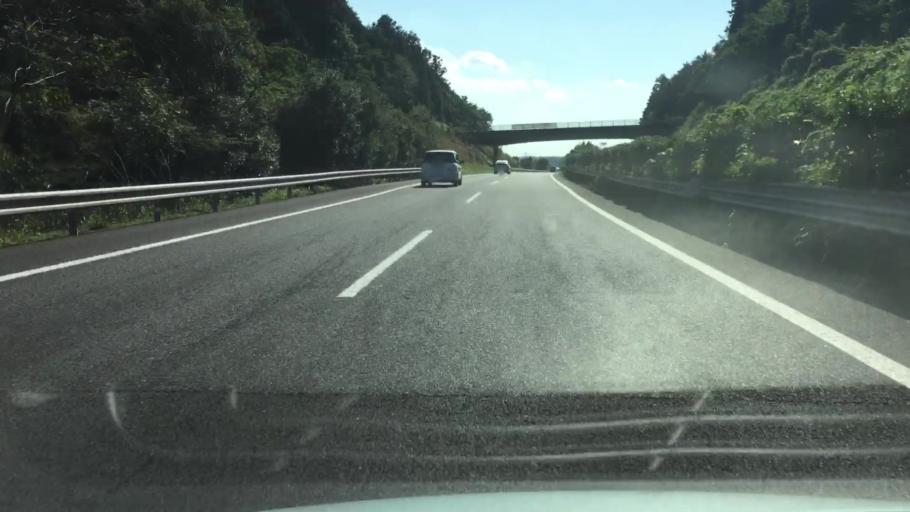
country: JP
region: Ibaraki
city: Tomobe
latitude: 36.3370
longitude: 140.2822
